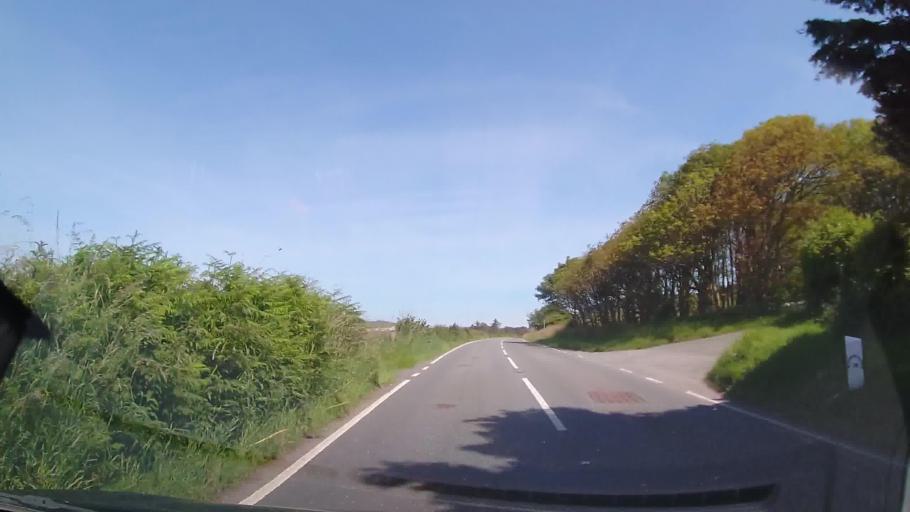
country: GB
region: Wales
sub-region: Gwynedd
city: Tywyn
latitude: 52.5640
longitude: -4.0722
